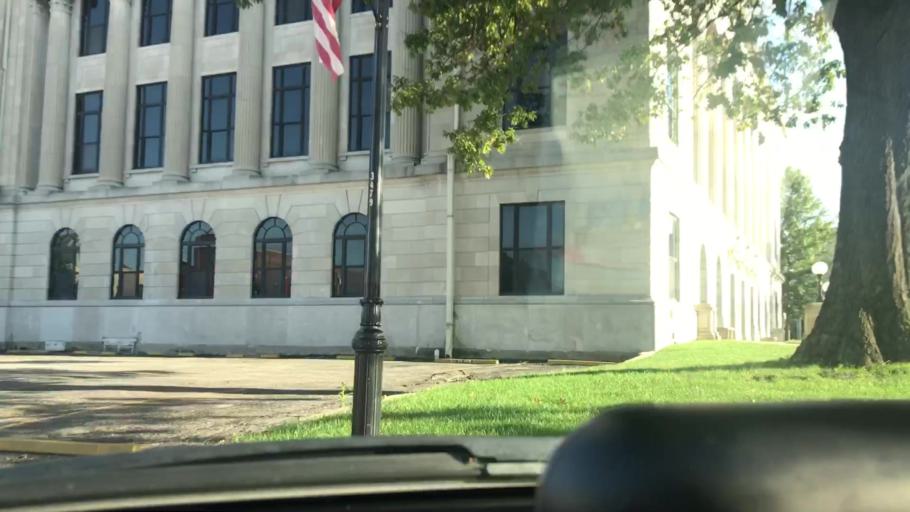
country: US
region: Missouri
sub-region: Pettis County
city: Sedalia
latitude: 38.7077
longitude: -93.2278
